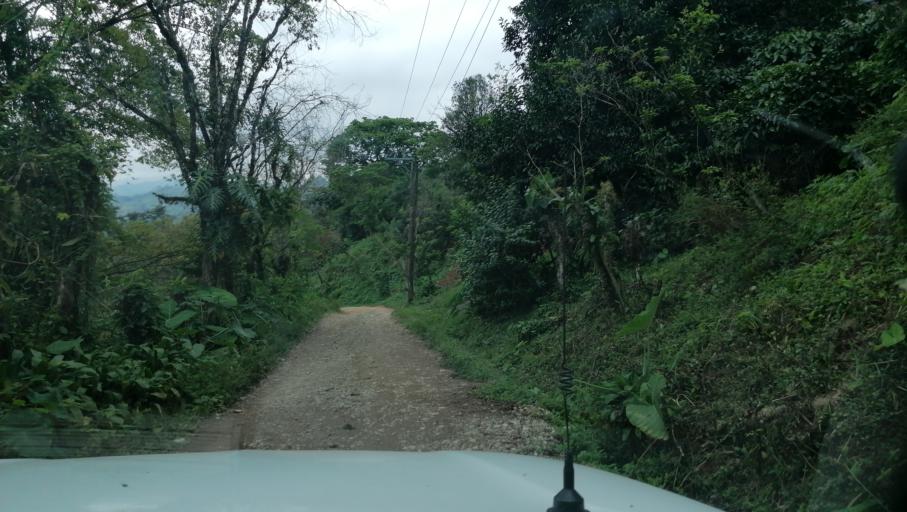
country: MX
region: Chiapas
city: Ixtacomitan
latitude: 17.3581
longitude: -93.1171
